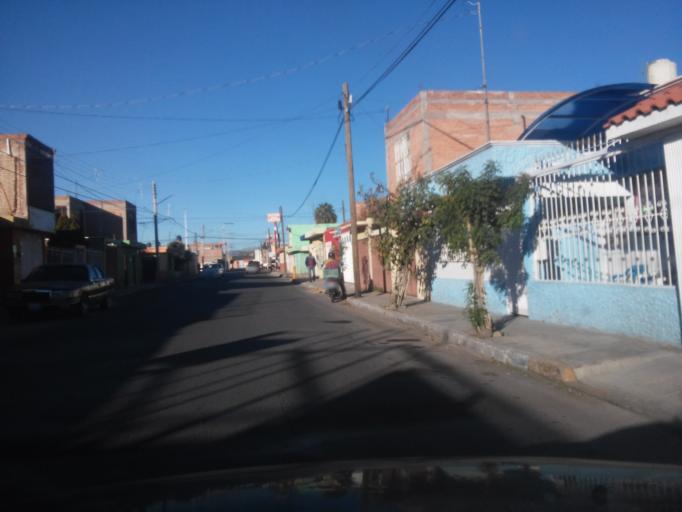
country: MX
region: Durango
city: Victoria de Durango
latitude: 24.0135
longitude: -104.6508
